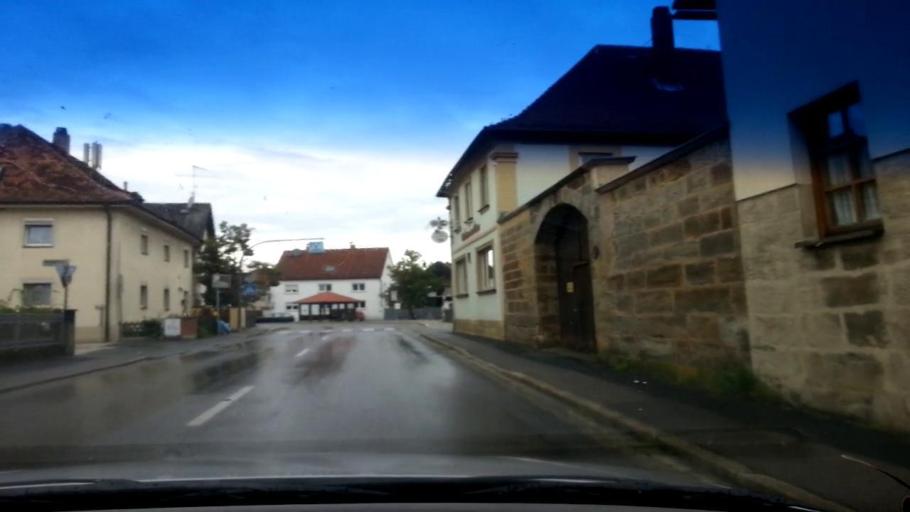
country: DE
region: Bavaria
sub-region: Upper Franconia
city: Hallstadt
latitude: 49.9293
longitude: 10.8701
